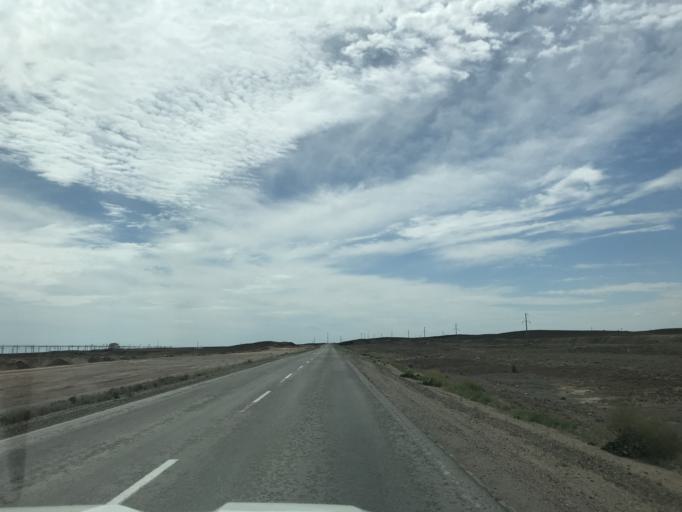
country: KZ
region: Almaty Oblysy
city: Ulken
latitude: 45.1822
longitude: 73.9233
